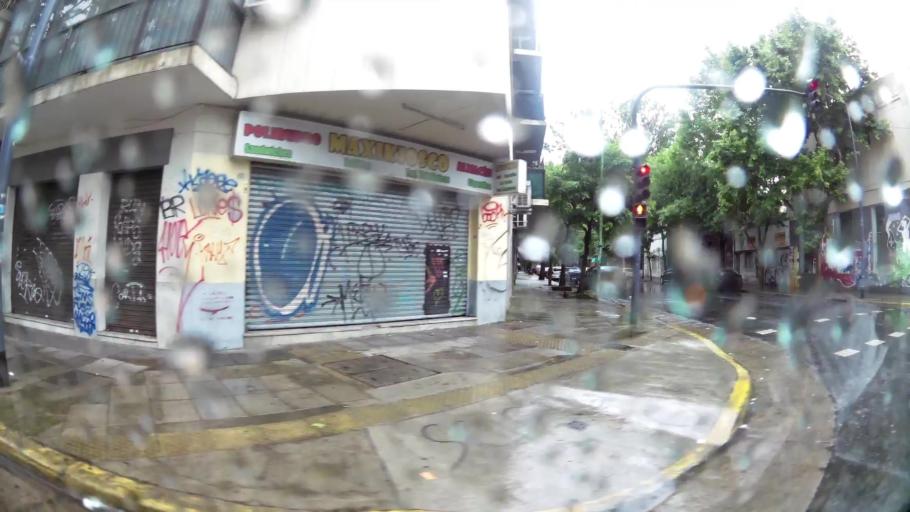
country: AR
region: Buenos Aires F.D.
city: Colegiales
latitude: -34.5889
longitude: -58.4362
